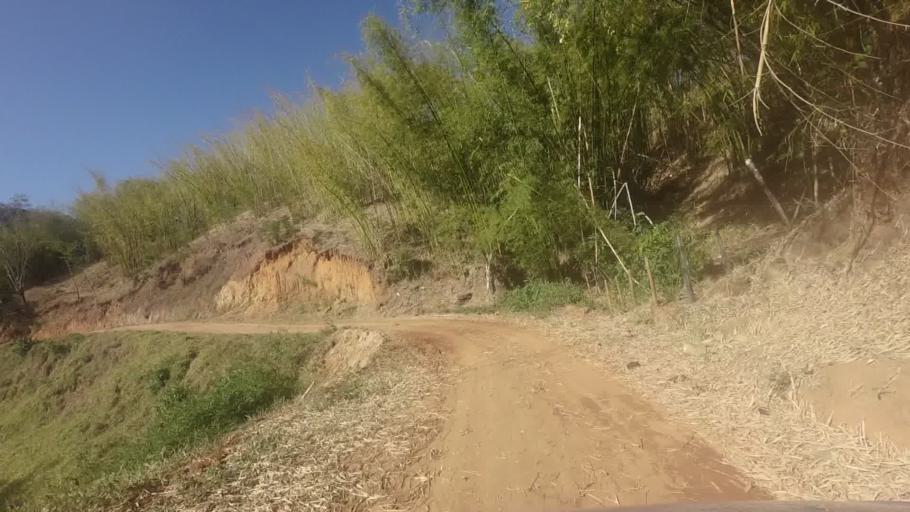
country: BR
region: Espirito Santo
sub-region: Sao Jose Do Calcado
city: Sao Jose do Calcado
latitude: -21.0376
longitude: -41.5999
